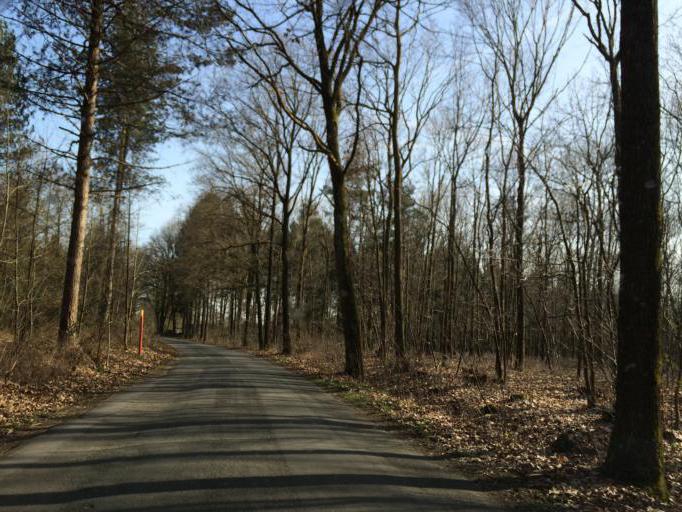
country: DE
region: North Rhine-Westphalia
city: Marl
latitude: 51.7018
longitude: 7.0299
